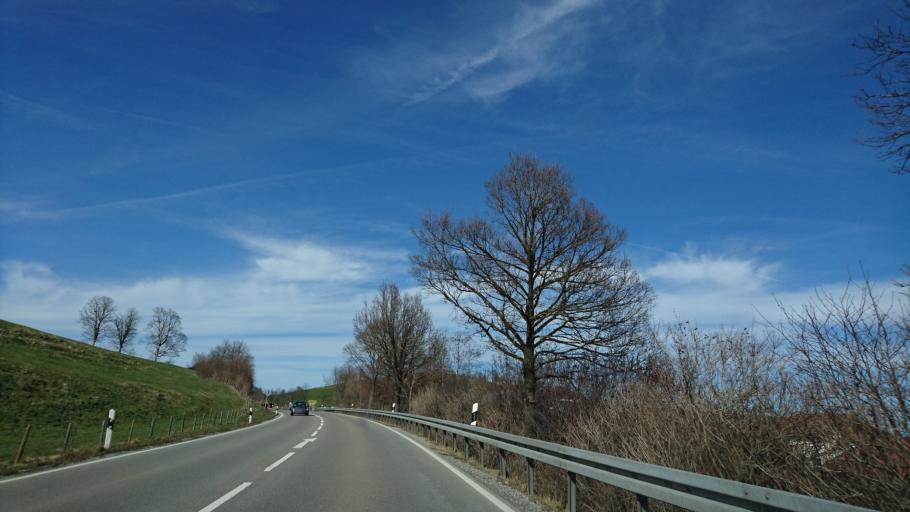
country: DE
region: Bavaria
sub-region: Swabia
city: Rosshaupten
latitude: 47.6120
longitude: 10.7146
